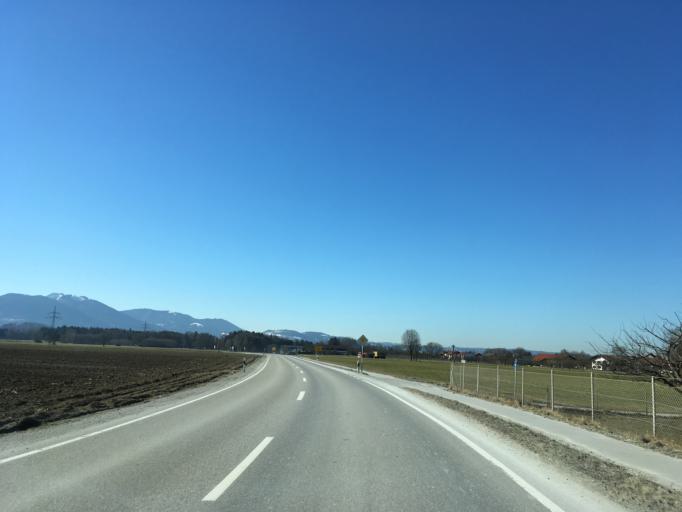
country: DE
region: Bavaria
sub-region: Upper Bavaria
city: Rohrdorf
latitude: 47.7938
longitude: 12.1777
